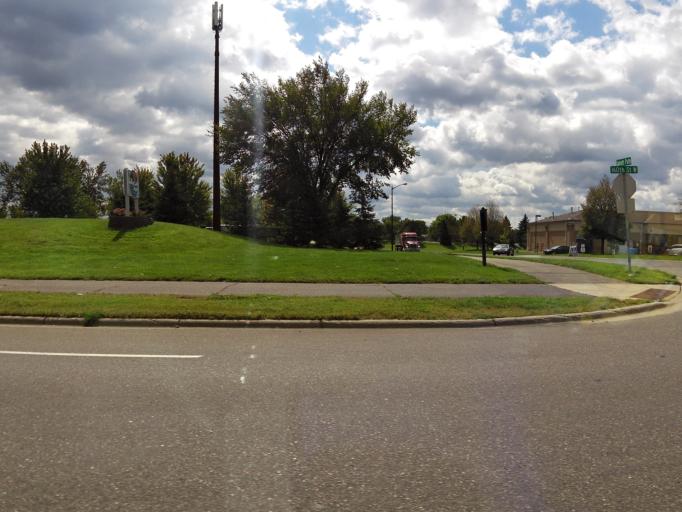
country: US
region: Minnesota
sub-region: Dakota County
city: Apple Valley
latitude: 44.7173
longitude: -93.2126
